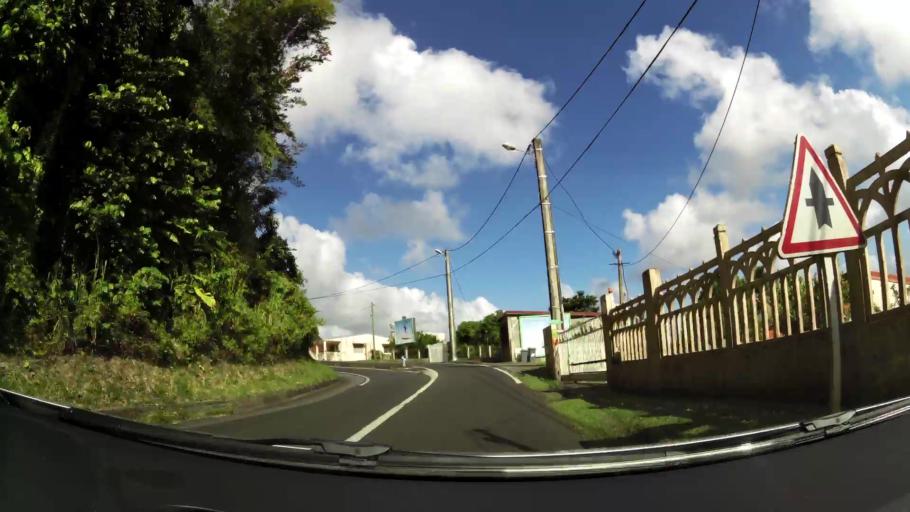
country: MQ
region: Martinique
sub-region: Martinique
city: Fort-de-France
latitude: 14.6487
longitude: -61.0783
